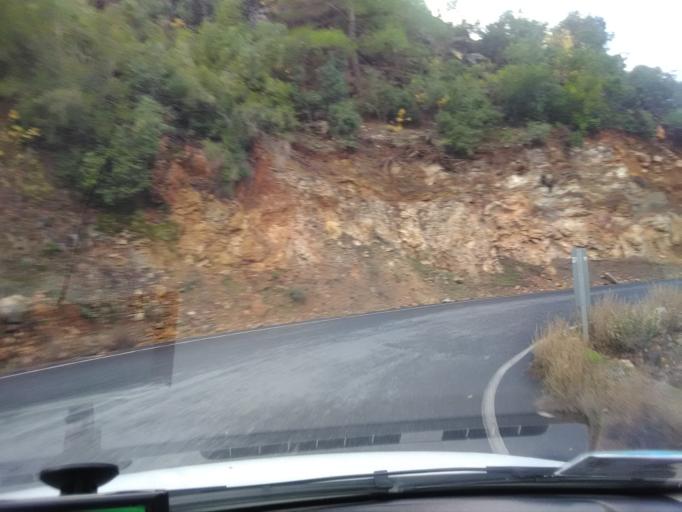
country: TR
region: Antalya
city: Gazipasa
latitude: 36.2884
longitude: 32.3765
